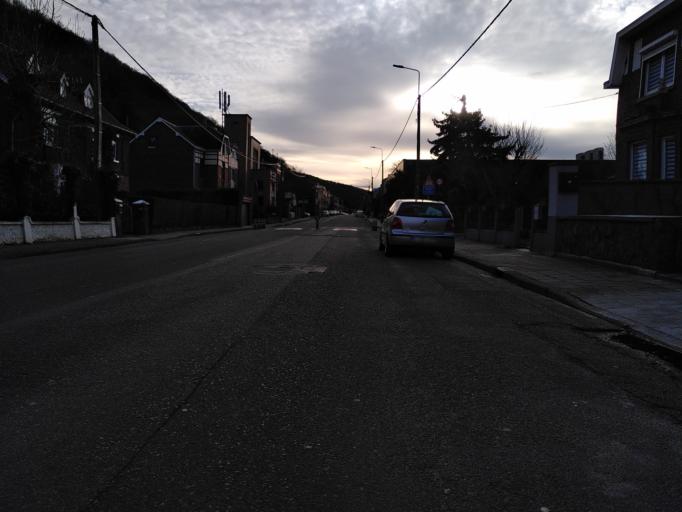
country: BE
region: Wallonia
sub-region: Province de Liege
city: Herstal
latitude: 50.6665
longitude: 5.6584
